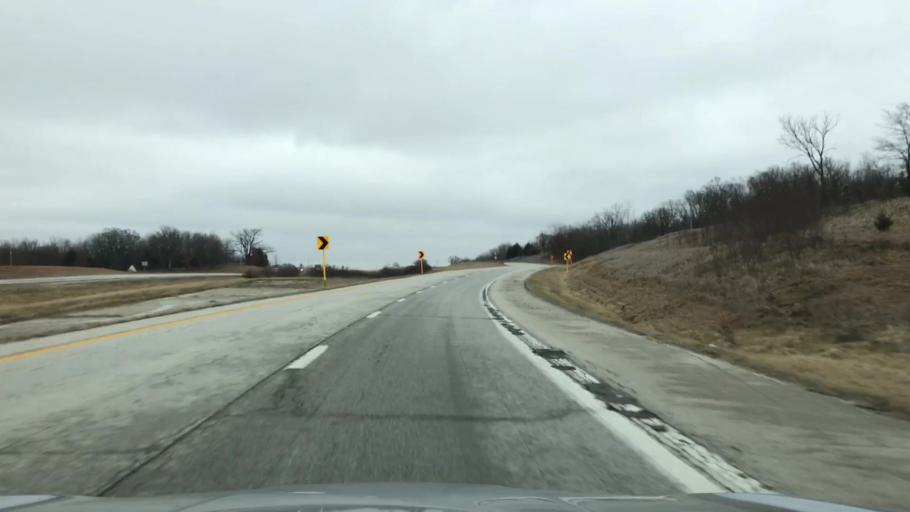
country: US
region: Missouri
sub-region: Linn County
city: Marceline
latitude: 39.7609
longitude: -92.9310
